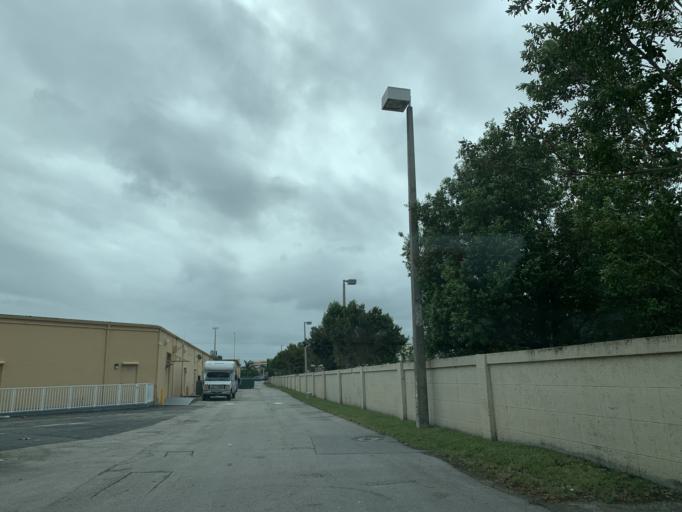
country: US
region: Florida
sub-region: Miami-Dade County
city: The Hammocks
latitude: 25.6856
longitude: -80.4560
